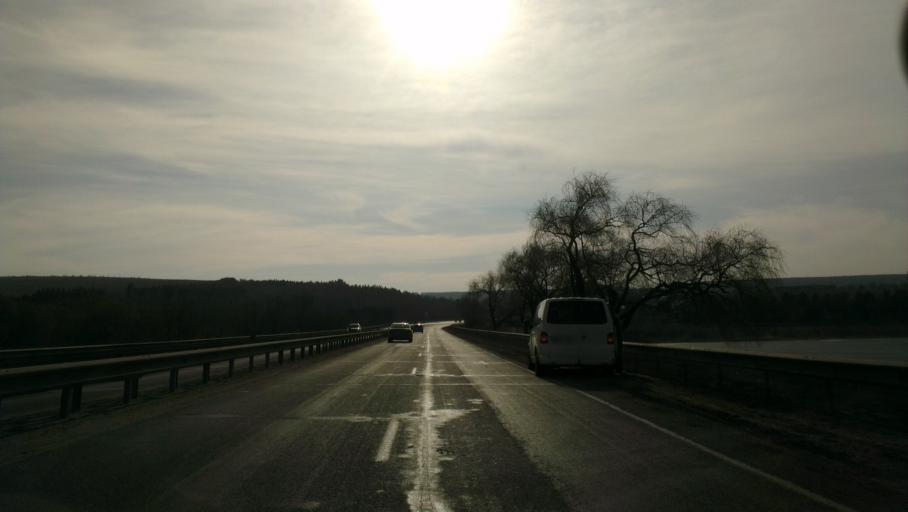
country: MD
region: Laloveni
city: Ialoveni
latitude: 46.9548
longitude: 28.7424
